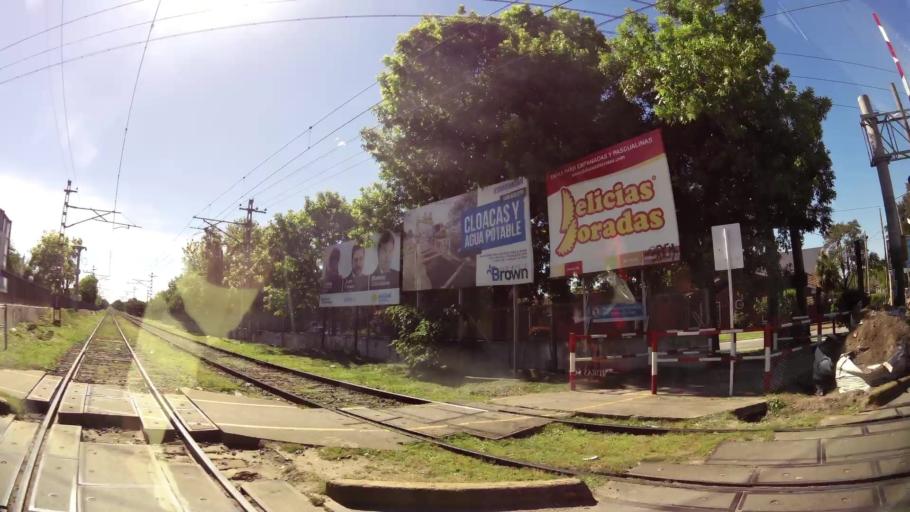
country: AR
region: Buenos Aires
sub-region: Partido de Almirante Brown
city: Adrogue
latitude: -34.7956
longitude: -58.3642
